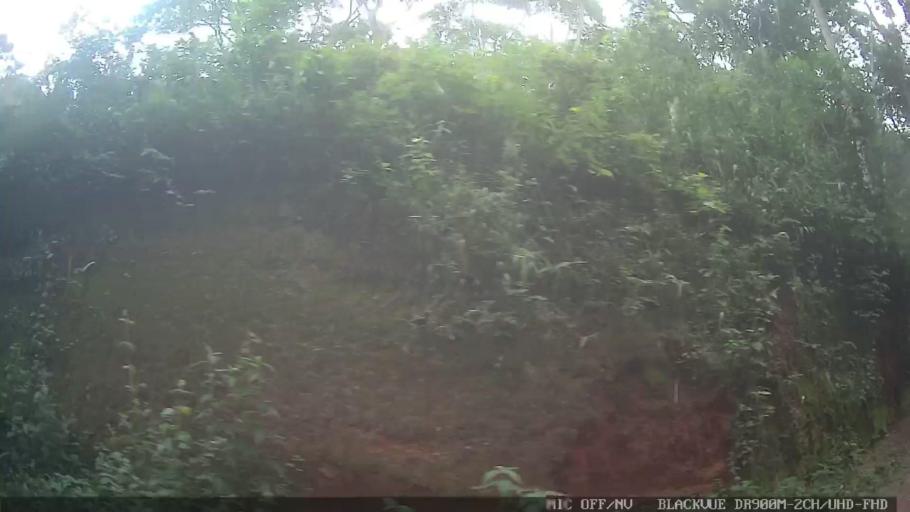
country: BR
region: Minas Gerais
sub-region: Extrema
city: Extrema
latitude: -22.8276
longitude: -46.2420
